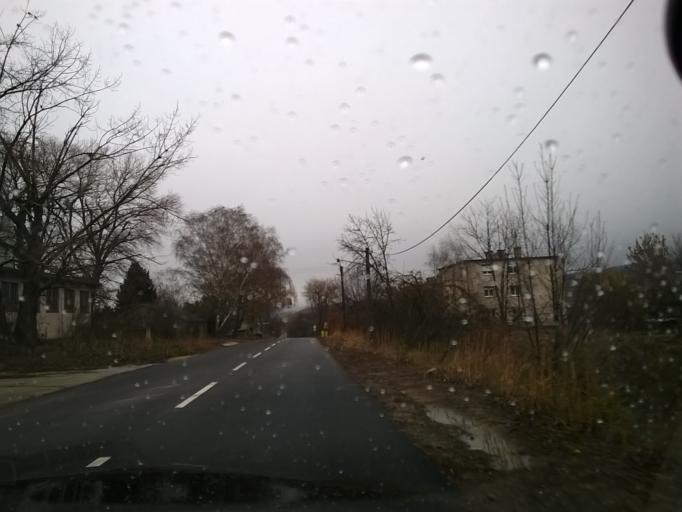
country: SK
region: Nitriansky
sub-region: Okres Nitra
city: Nitra
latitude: 48.3337
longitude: 18.0204
